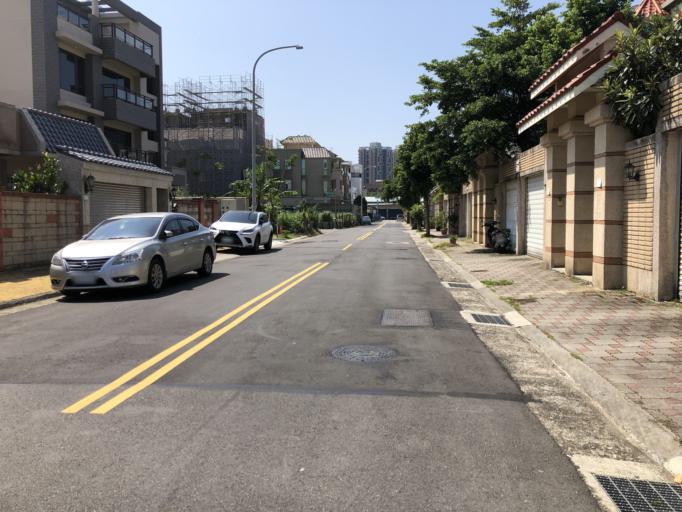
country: TW
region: Taipei
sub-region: Taipei
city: Banqiao
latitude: 25.0746
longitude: 121.3844
